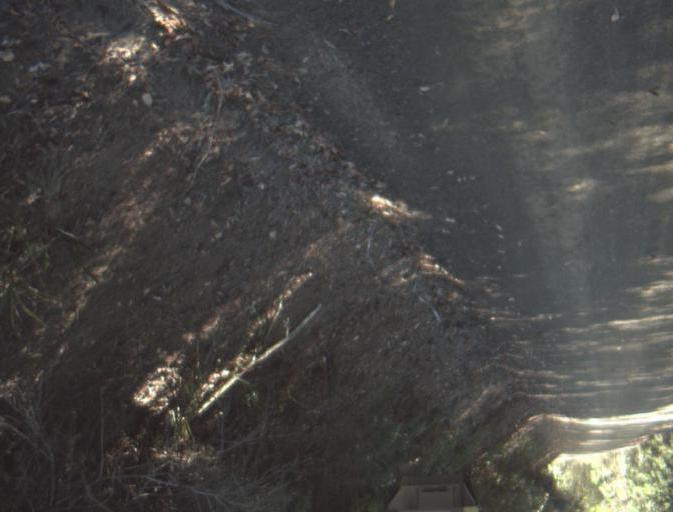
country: AU
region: Tasmania
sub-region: Dorset
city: Scottsdale
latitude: -41.2832
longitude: 147.3392
